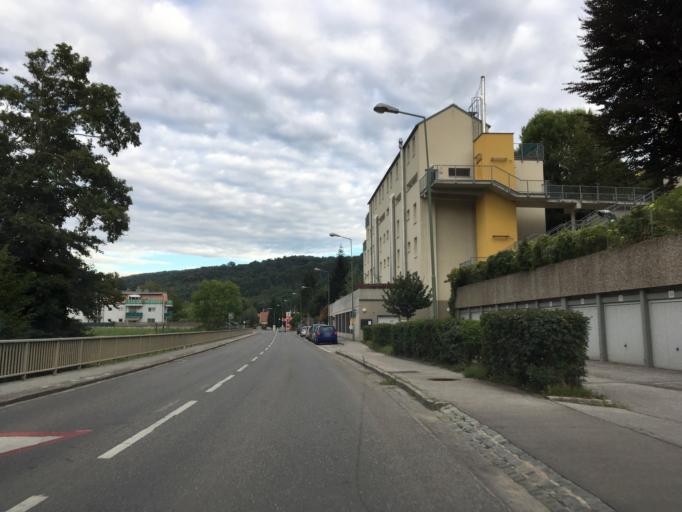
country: AT
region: Lower Austria
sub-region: Politischer Bezirk Wien-Umgebung
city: Klosterneuburg
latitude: 48.3075
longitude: 16.2859
